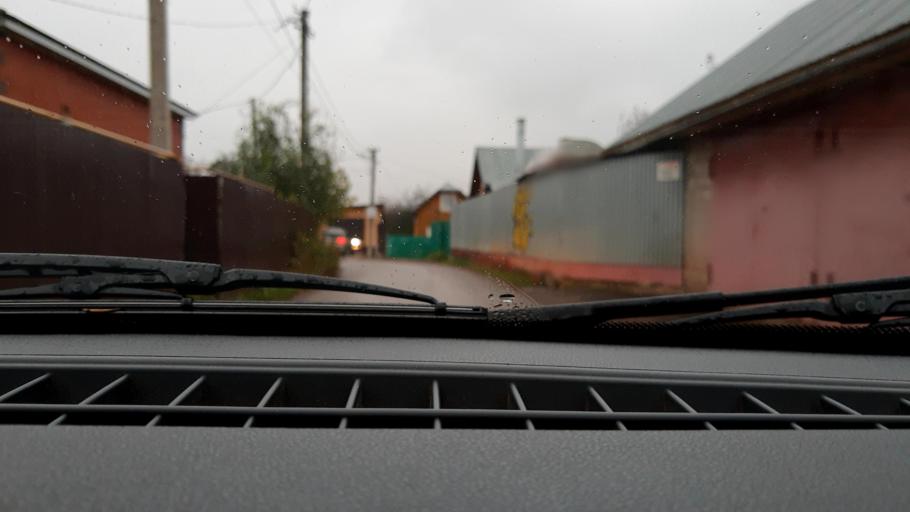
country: RU
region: Bashkortostan
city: Mikhaylovka
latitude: 54.7805
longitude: 55.8919
